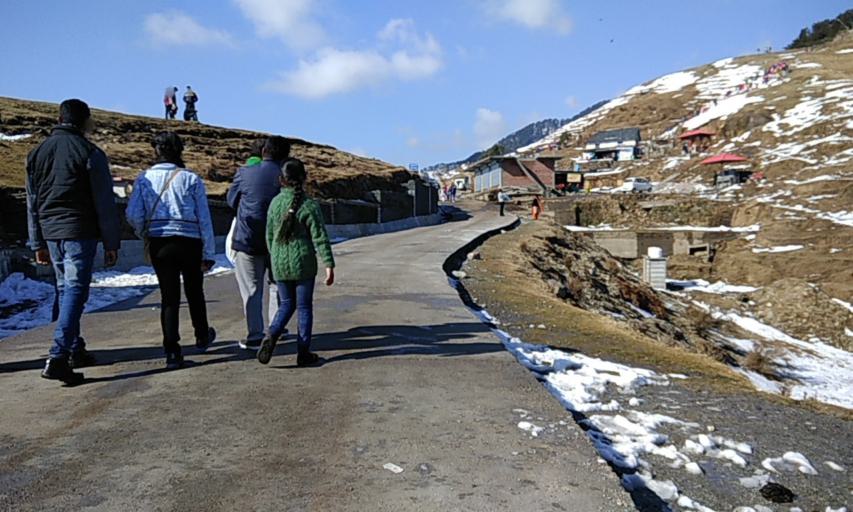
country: IN
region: Himachal Pradesh
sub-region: Mandi
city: Jogindarnagar
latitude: 32.0578
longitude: 76.7444
